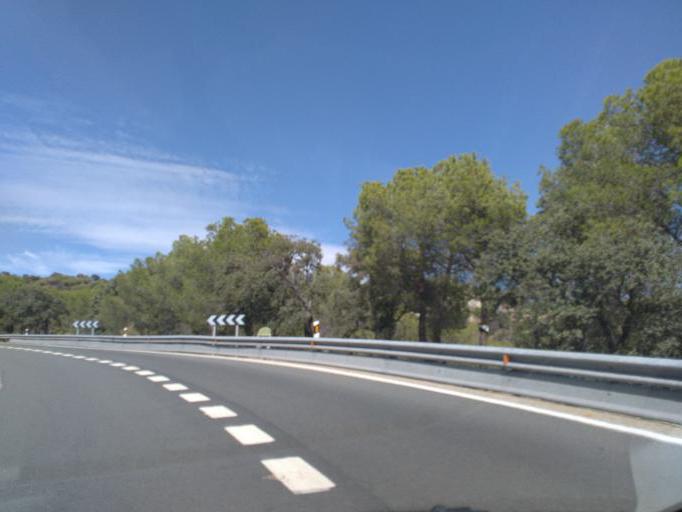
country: ES
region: Madrid
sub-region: Provincia de Madrid
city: Torrelodones
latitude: 40.5449
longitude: -3.9585
